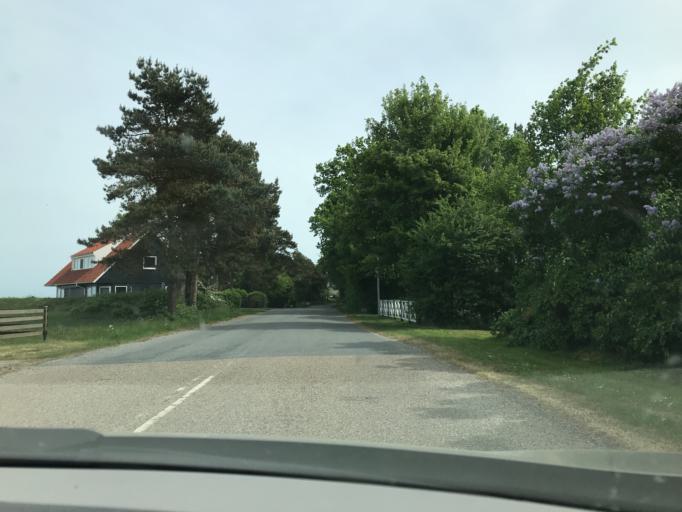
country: DK
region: Central Jutland
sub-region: Norddjurs Kommune
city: Allingabro
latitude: 56.6039
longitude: 10.3052
